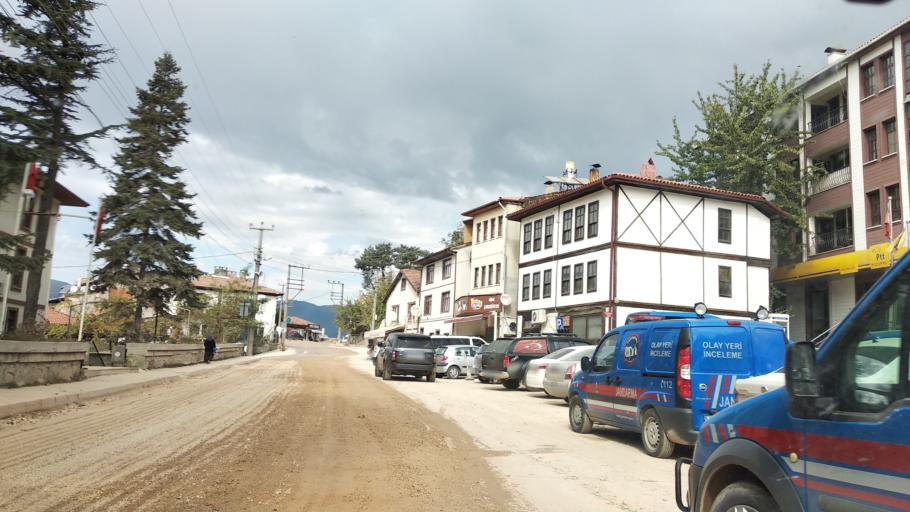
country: TR
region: Bolu
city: Mudurnu
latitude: 40.4683
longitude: 31.2102
